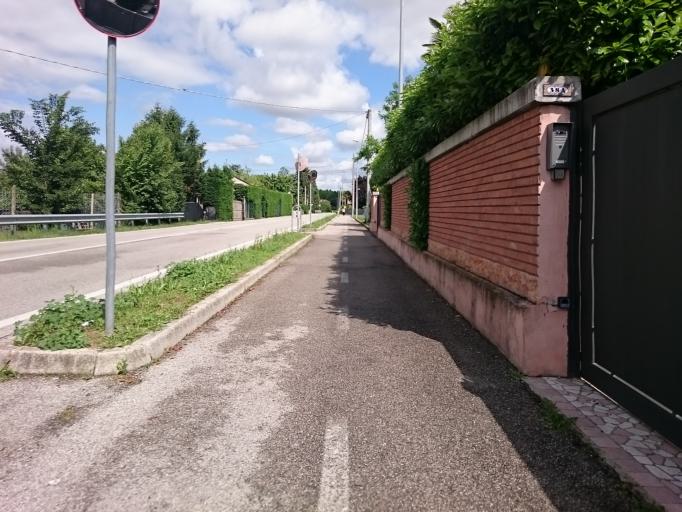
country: IT
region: Veneto
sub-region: Provincia di Padova
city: Mestrino
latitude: 45.4480
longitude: 11.7565
